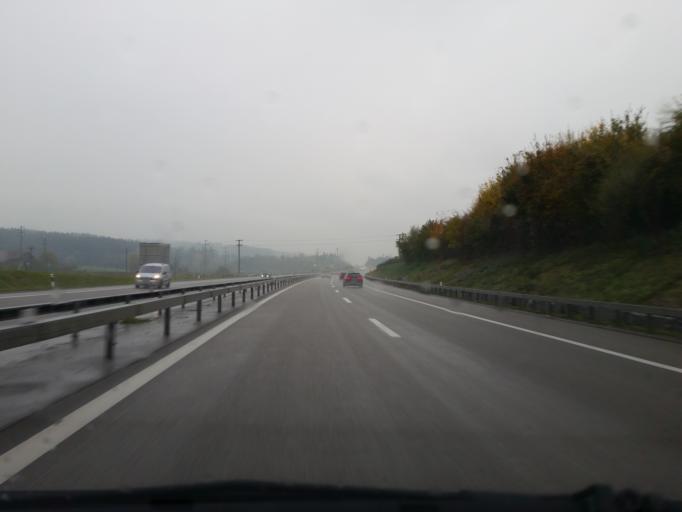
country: CH
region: Thurgau
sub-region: Frauenfeld District
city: Gachnang
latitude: 47.5454
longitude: 8.8213
